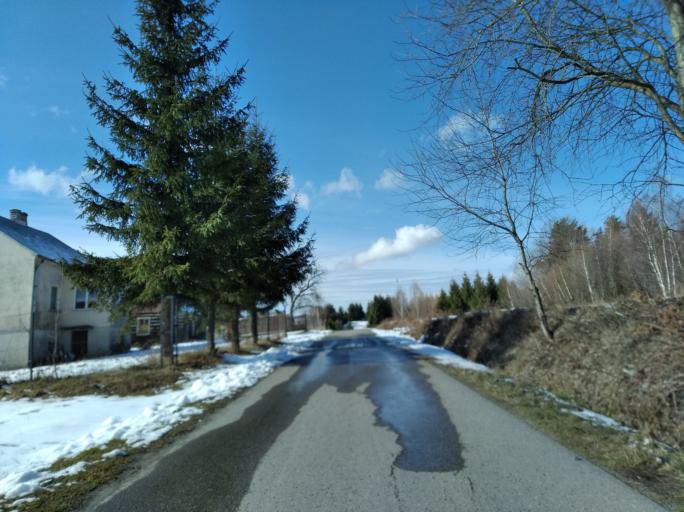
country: PL
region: Subcarpathian Voivodeship
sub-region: Powiat krosnienski
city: Korczyna
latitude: 49.7365
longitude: 21.8439
